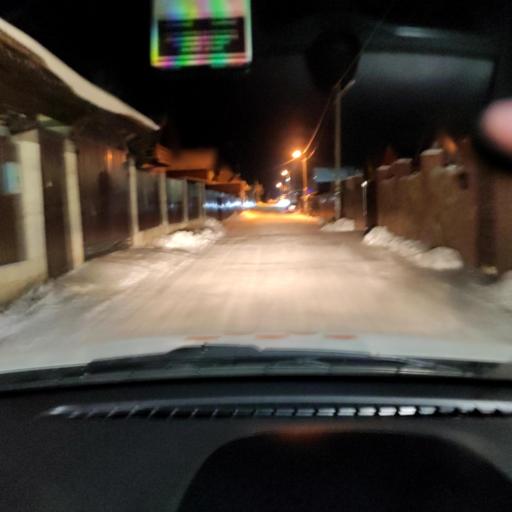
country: RU
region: Tatarstan
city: Vysokaya Gora
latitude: 55.8071
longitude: 49.3854
